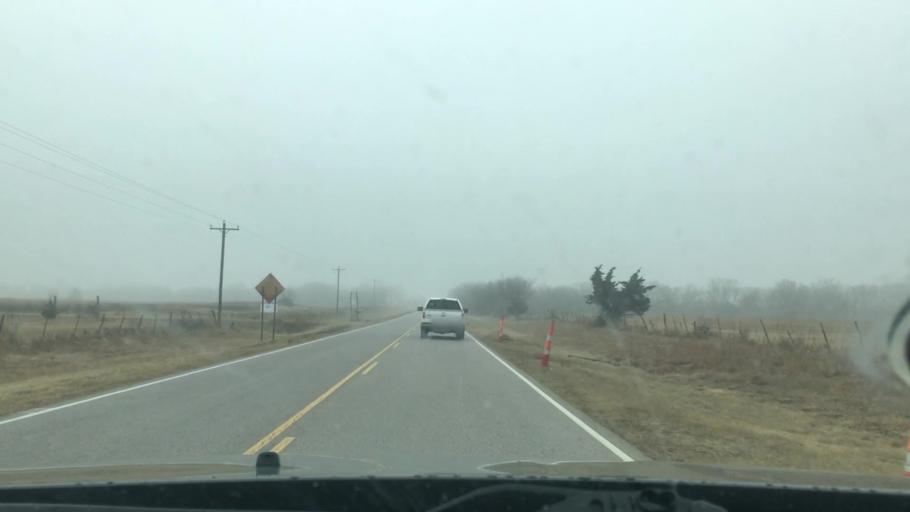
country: US
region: Oklahoma
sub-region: Johnston County
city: Tishomingo
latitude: 34.3157
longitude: -96.6710
